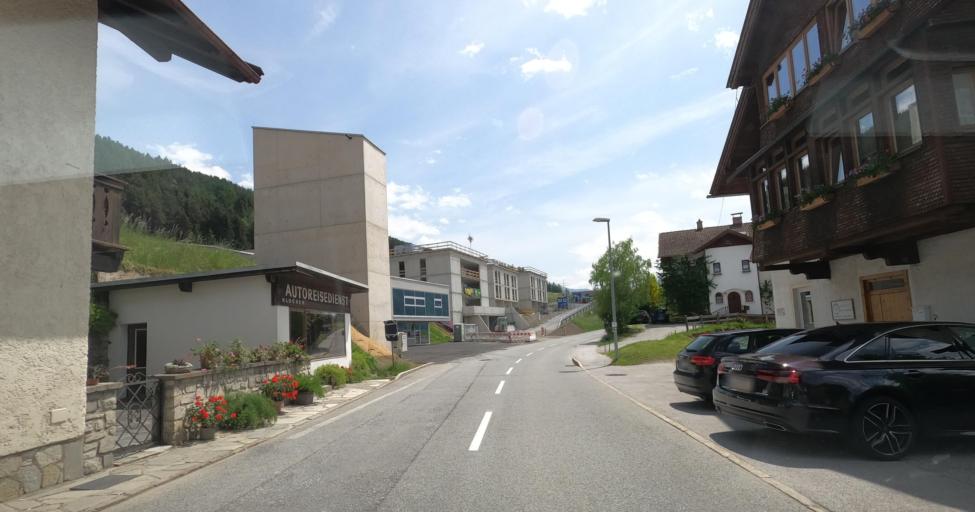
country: AT
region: Tyrol
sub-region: Politischer Bezirk Innsbruck Land
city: Patsch
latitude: 47.2044
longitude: 11.4169
